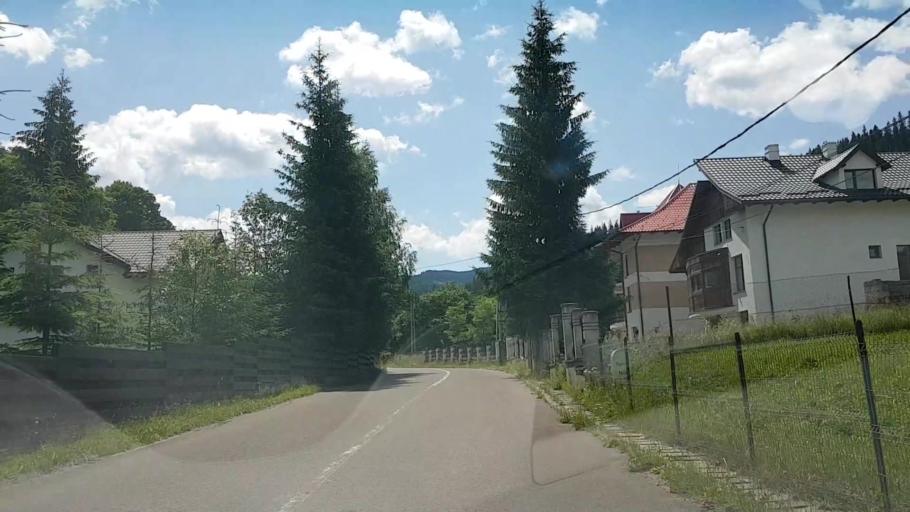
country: RO
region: Suceava
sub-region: Comuna Pojorata
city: Pojorata
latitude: 47.4938
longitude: 25.4837
